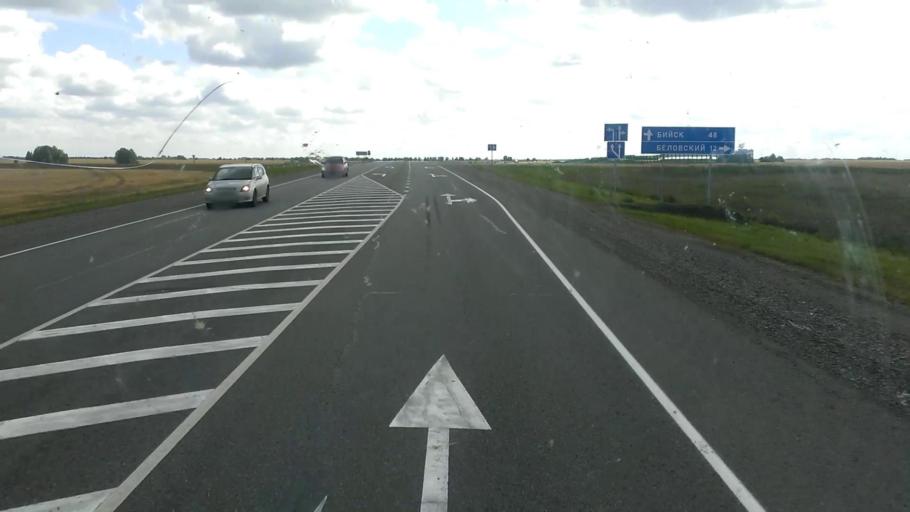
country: RU
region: Altai Krai
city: Troitskoye
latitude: 52.9175
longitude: 84.8111
